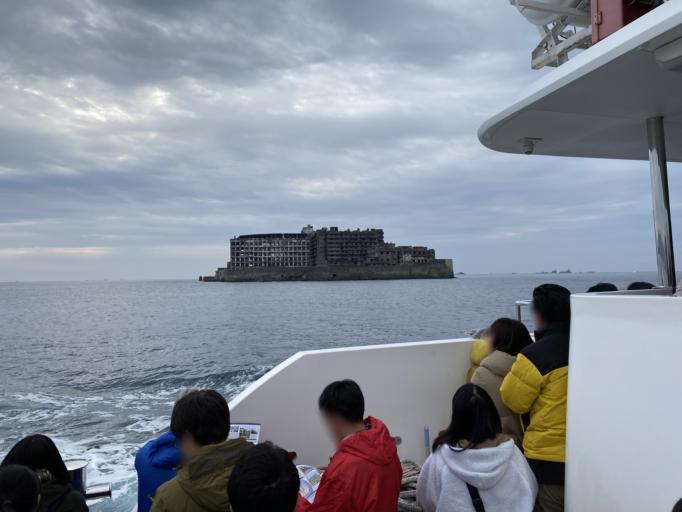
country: JP
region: Nagasaki
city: Nagasaki-shi
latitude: 32.6320
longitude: 129.7401
